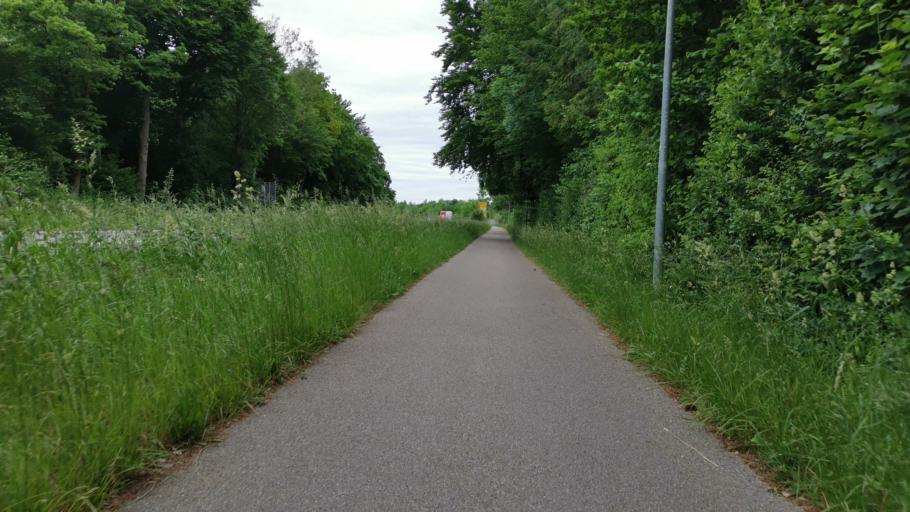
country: DE
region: Bavaria
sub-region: Upper Bavaria
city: Neuried
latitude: 48.1003
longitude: 11.4478
